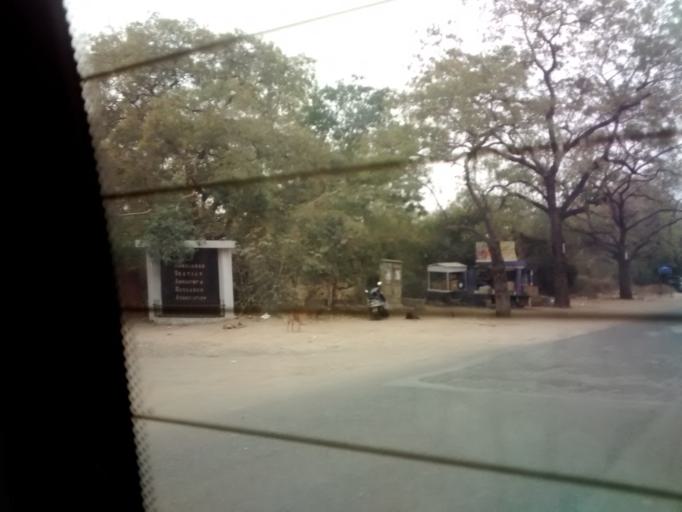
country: IN
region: Gujarat
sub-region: Ahmadabad
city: Ahmedabad
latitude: 23.0350
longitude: 72.5429
